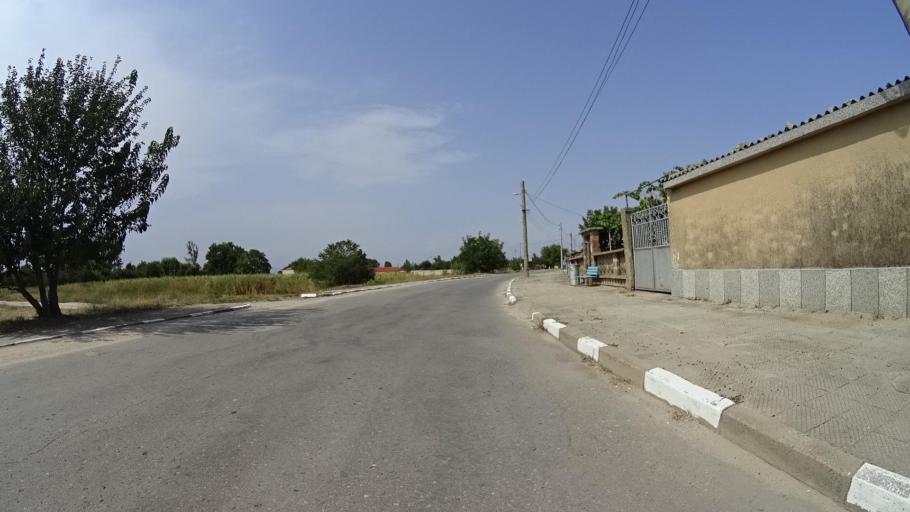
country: BG
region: Plovdiv
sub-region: Obshtina Plovdiv
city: Plovdiv
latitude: 42.2437
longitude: 24.7951
